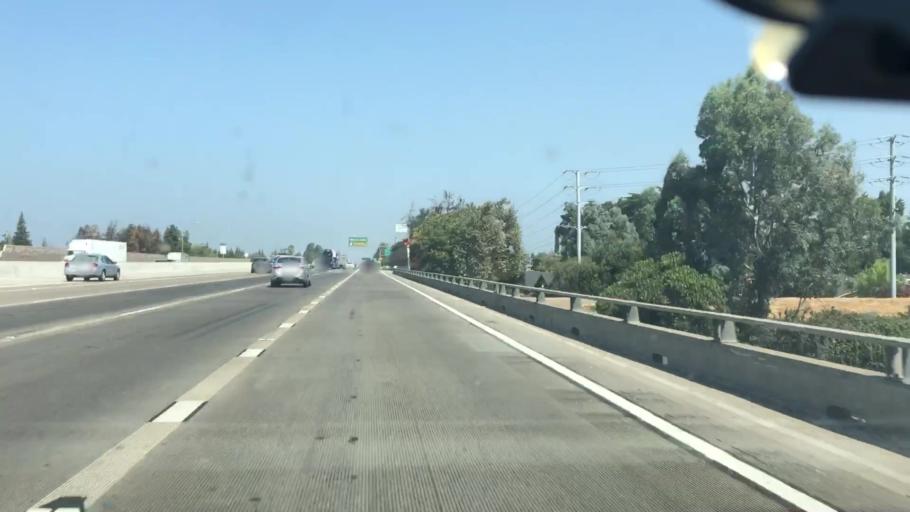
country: US
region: California
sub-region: San Joaquin County
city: Country Club
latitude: 37.9791
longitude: -121.3410
